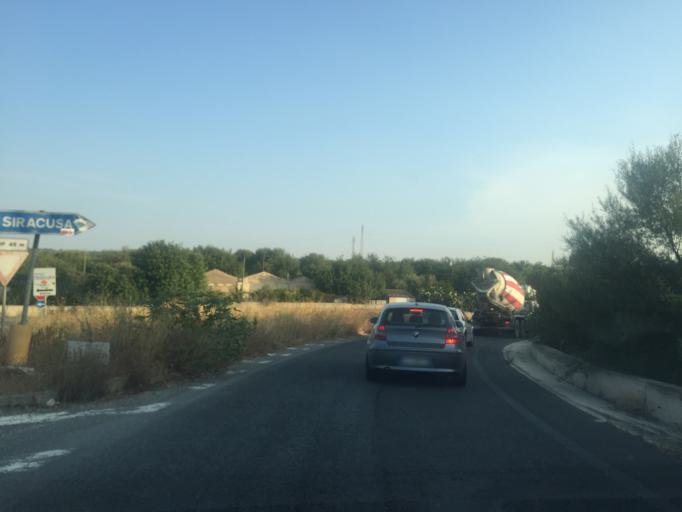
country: IT
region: Sicily
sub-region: Ragusa
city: Pozzallo
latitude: 36.7473
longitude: 14.8747
